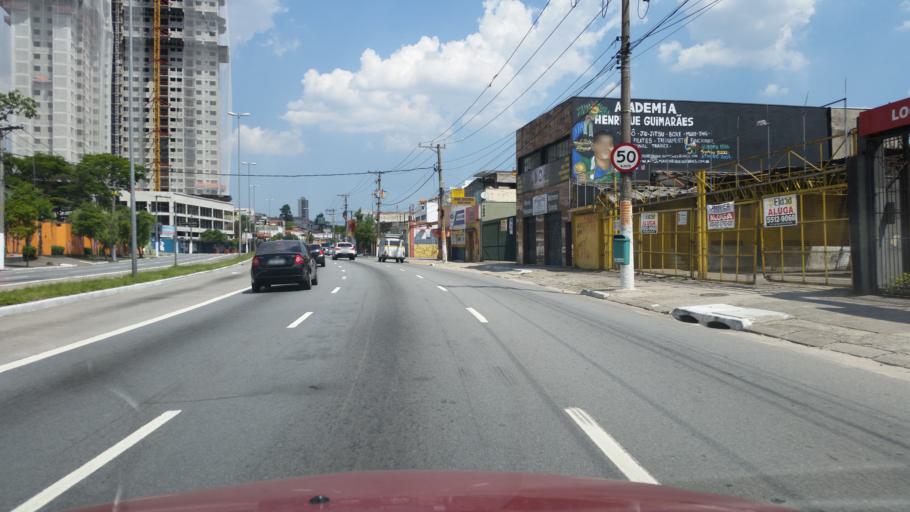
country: BR
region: Sao Paulo
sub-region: Diadema
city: Diadema
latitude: -23.6536
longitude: -46.6685
